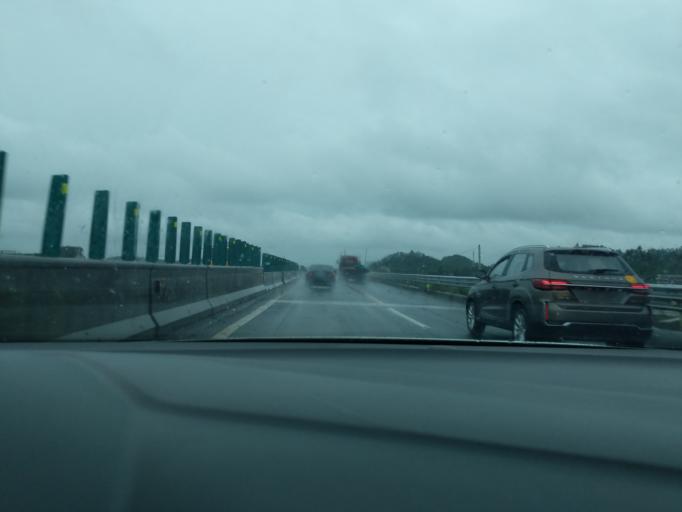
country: CN
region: Guangdong
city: Yueshan
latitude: 22.4628
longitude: 112.7185
